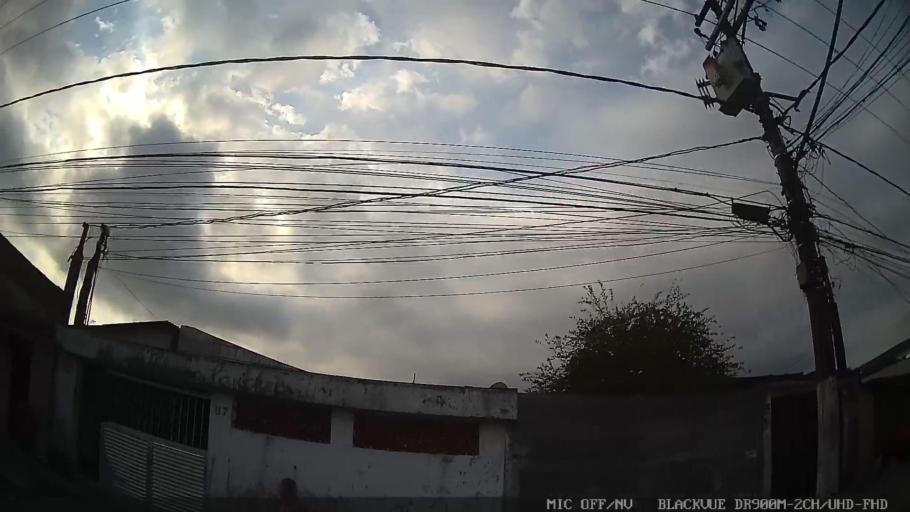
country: BR
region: Sao Paulo
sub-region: Guaruja
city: Guaruja
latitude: -23.9553
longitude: -46.2787
